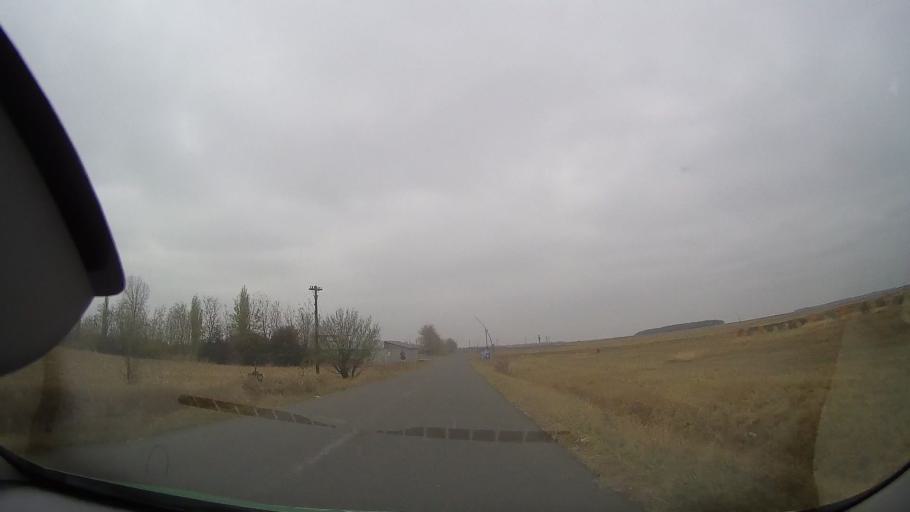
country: RO
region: Buzau
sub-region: Comuna Scutelnici
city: Scutelnici
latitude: 44.8532
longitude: 26.9096
